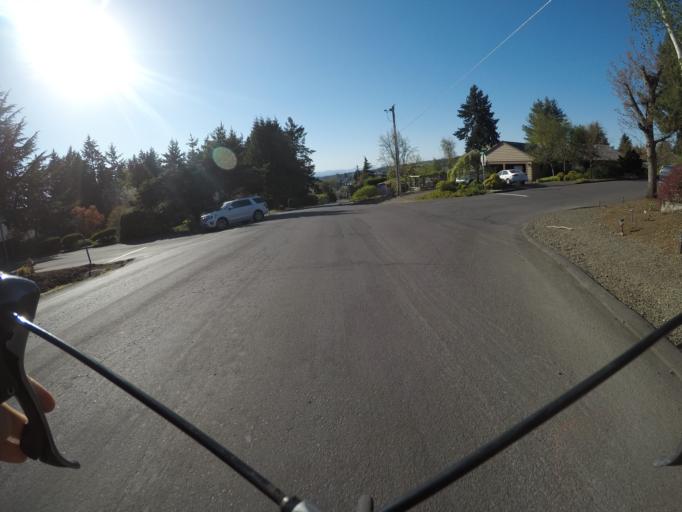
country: US
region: Oregon
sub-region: Washington County
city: King City
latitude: 45.4181
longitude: -122.8394
